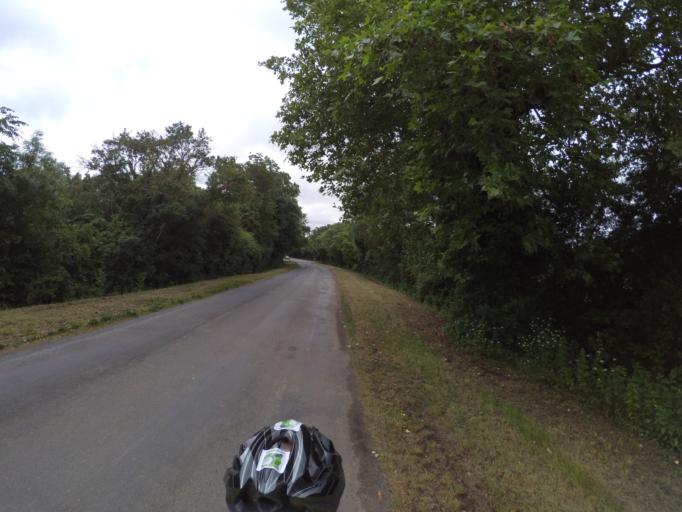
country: FR
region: Poitou-Charentes
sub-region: Departement de la Charente-Maritime
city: Saint-Laurent-de-la-Pree
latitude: 45.9945
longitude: -1.0347
